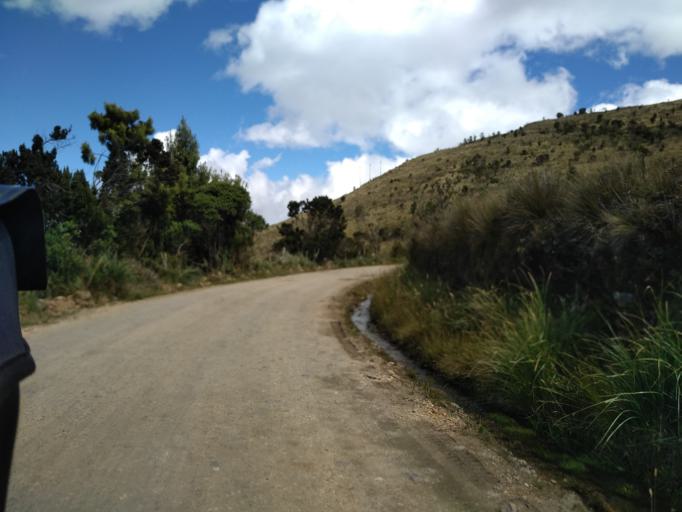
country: CO
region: Boyaca
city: Duitama
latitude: 5.9339
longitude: -73.0933
